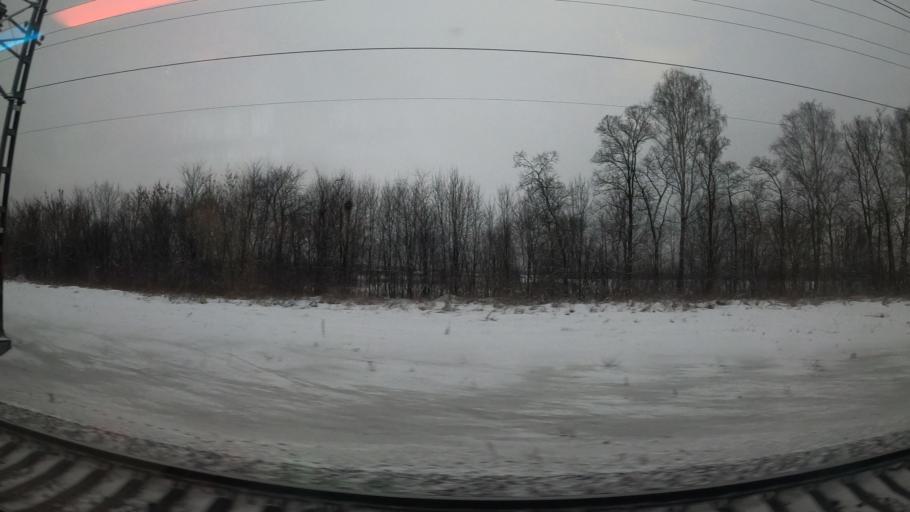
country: RU
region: Vladimir
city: Aleksandrov
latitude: 56.4101
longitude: 38.7542
